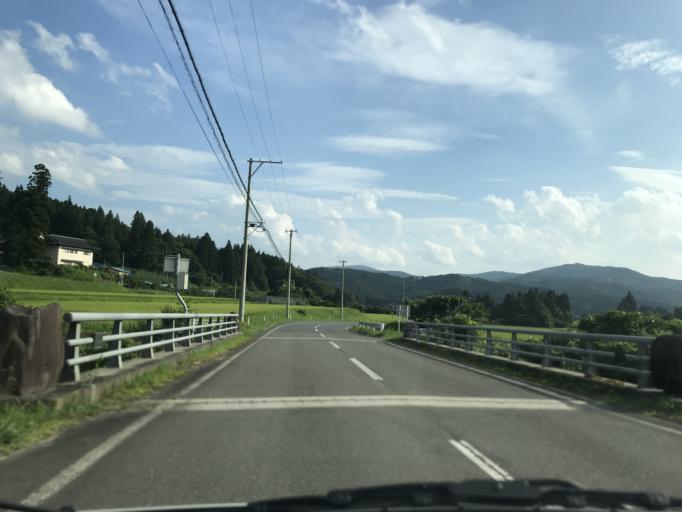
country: JP
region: Iwate
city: Ofunato
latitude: 38.9482
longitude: 141.4622
